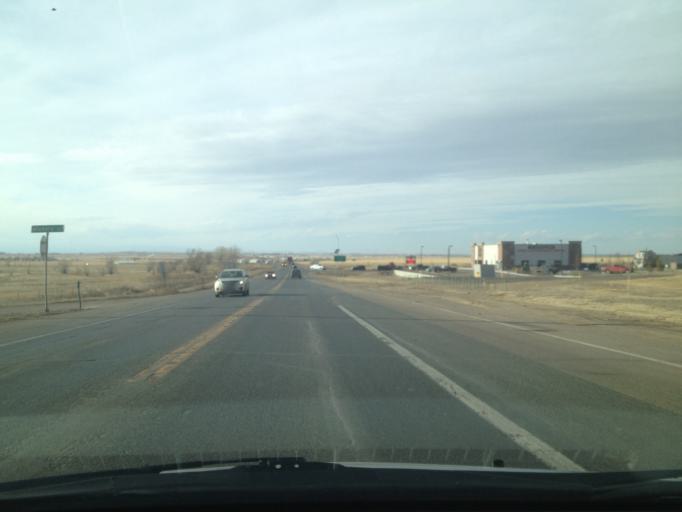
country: US
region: Colorado
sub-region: Weld County
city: Hudson
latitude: 40.0767
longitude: -104.6494
